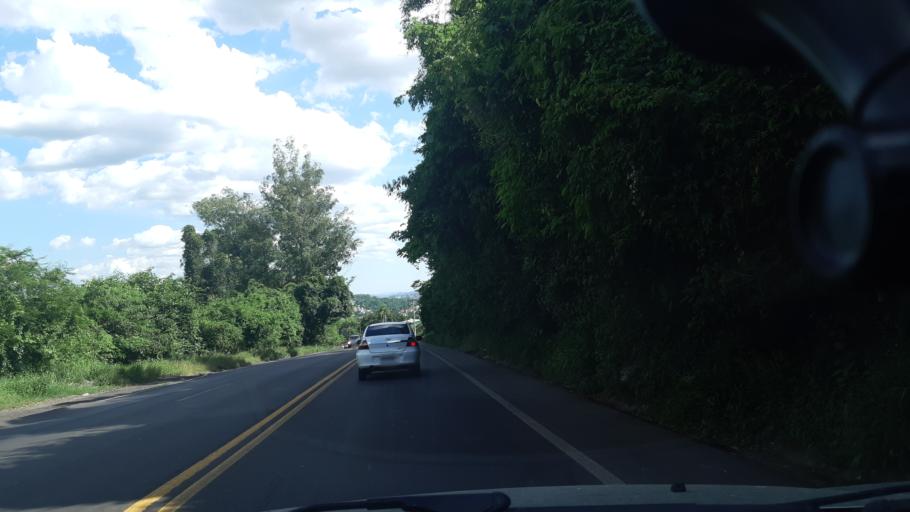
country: BR
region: Rio Grande do Sul
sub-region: Estancia Velha
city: Estancia Velha
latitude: -29.6301
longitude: -51.1438
